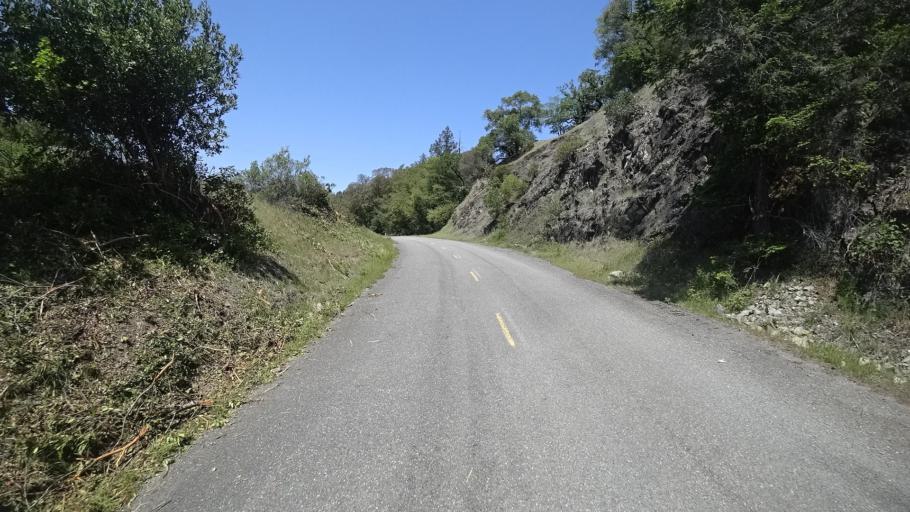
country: US
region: California
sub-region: Humboldt County
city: Redway
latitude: 40.2191
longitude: -123.6319
